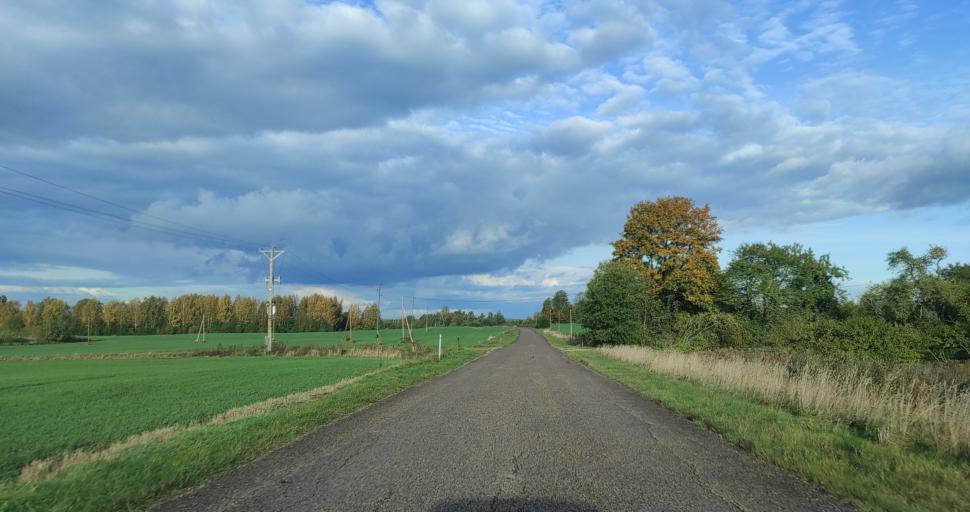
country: LV
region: Aizpute
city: Aizpute
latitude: 56.7776
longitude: 21.7786
